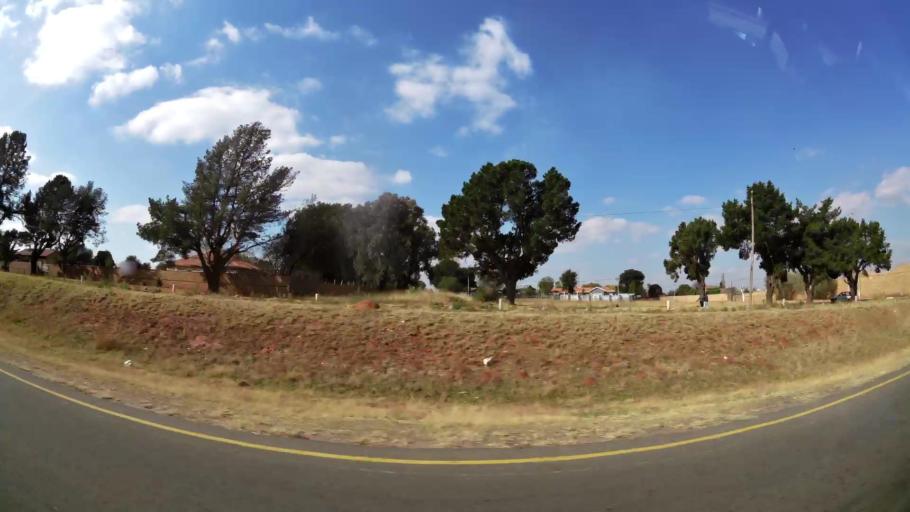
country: ZA
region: Gauteng
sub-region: West Rand District Municipality
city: Krugersdorp
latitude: -26.0854
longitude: 27.7597
